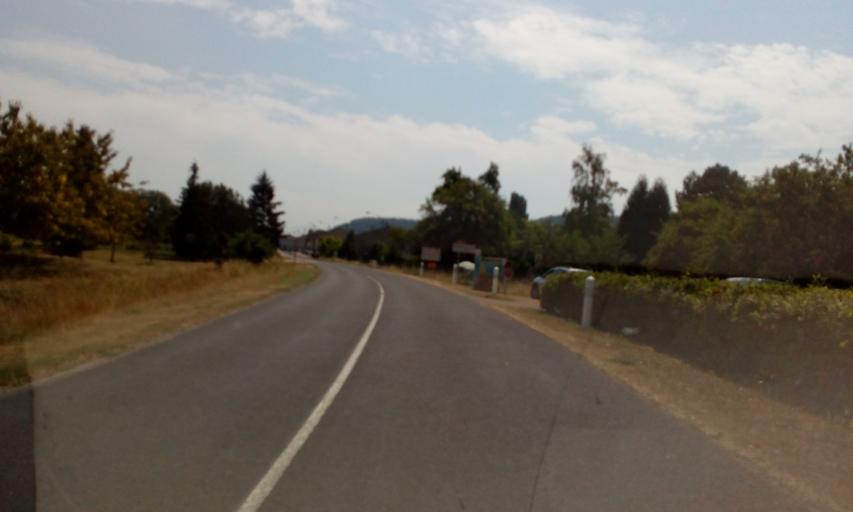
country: FR
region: Lorraine
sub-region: Departement de la Meuse
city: Vigneulles-les-Hattonchatel
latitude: 49.0418
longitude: 5.6539
